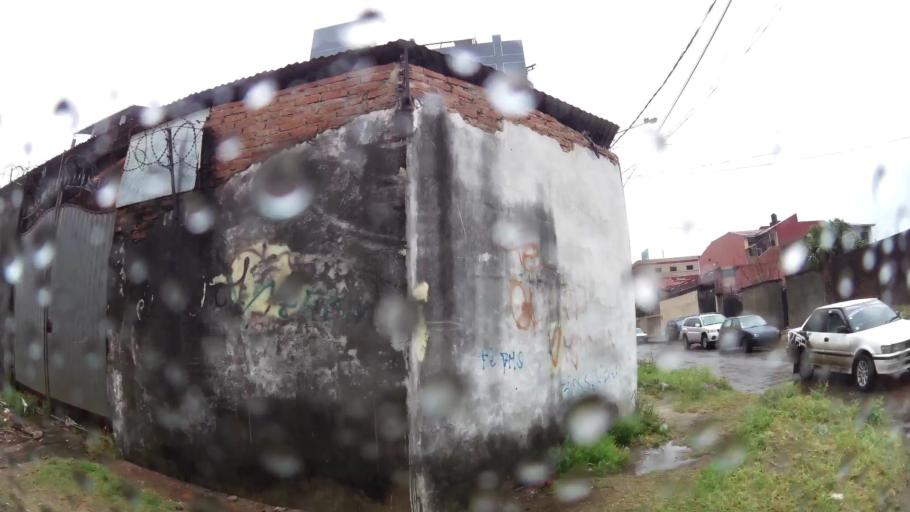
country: BO
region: Santa Cruz
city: Santa Cruz de la Sierra
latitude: -17.7838
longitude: -63.1575
